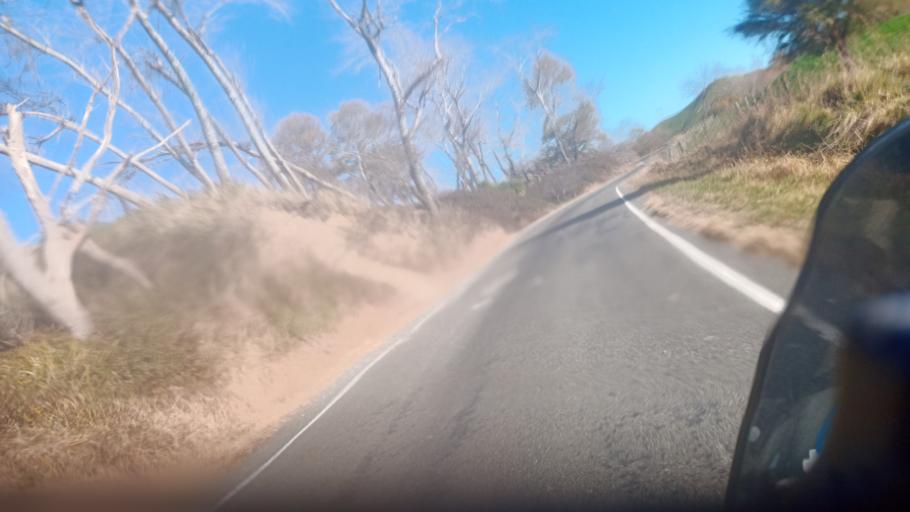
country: NZ
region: Gisborne
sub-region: Gisborne District
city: Gisborne
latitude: -38.5764
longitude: 177.5770
